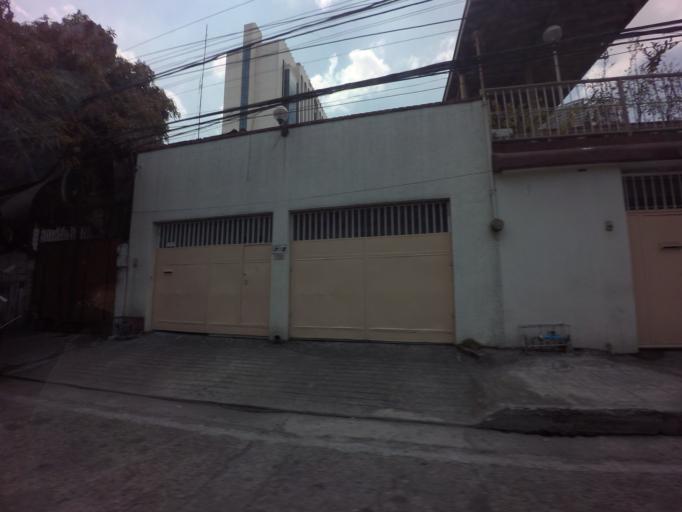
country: PH
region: Metro Manila
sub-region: Mandaluyong
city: Mandaluyong City
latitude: 14.5708
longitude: 121.0261
